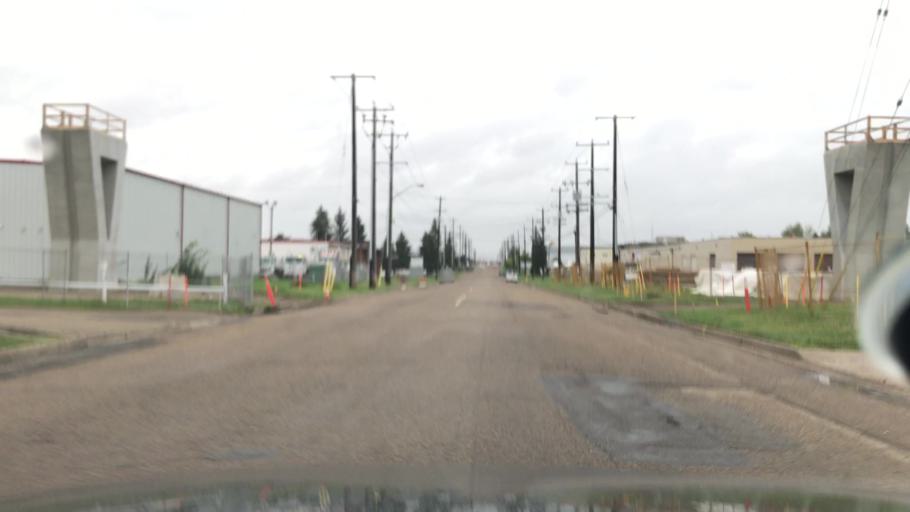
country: CA
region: Alberta
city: Edmonton
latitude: 53.5028
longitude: -113.4514
